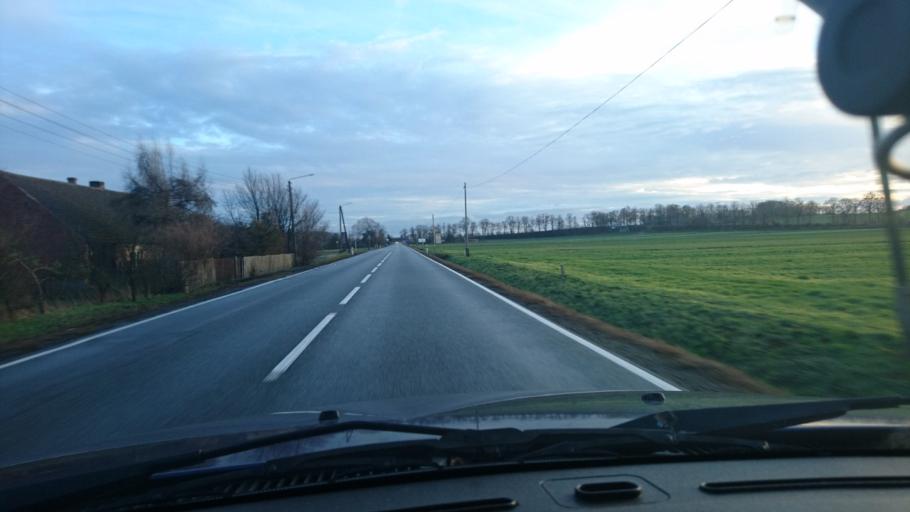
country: PL
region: Opole Voivodeship
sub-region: Powiat kluczborski
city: Byczyna
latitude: 51.1414
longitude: 18.1948
